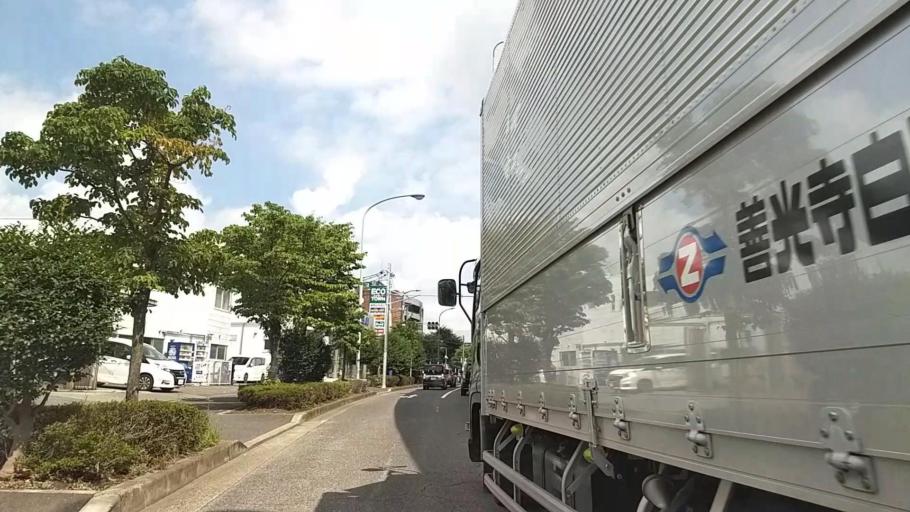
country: JP
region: Tokyo
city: Hachioji
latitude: 35.6618
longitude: 139.3531
